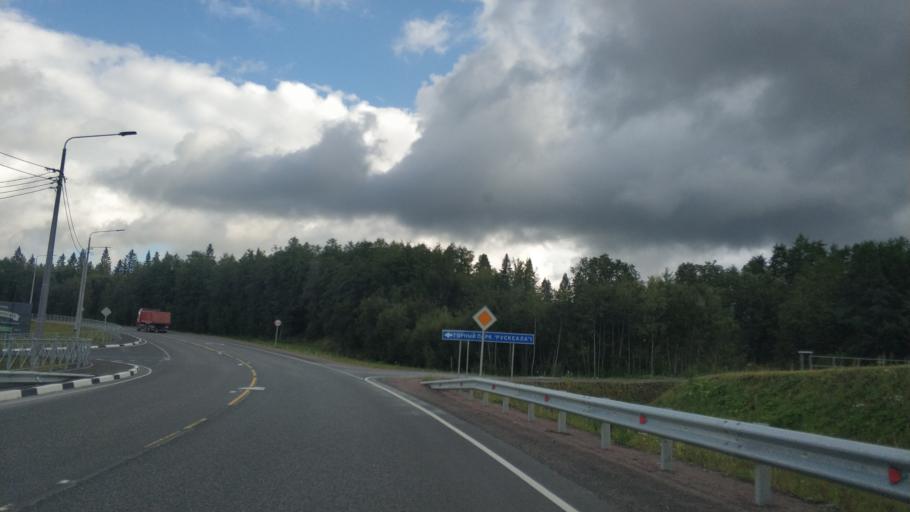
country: RU
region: Republic of Karelia
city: Ruskeala
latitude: 61.9457
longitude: 30.5985
